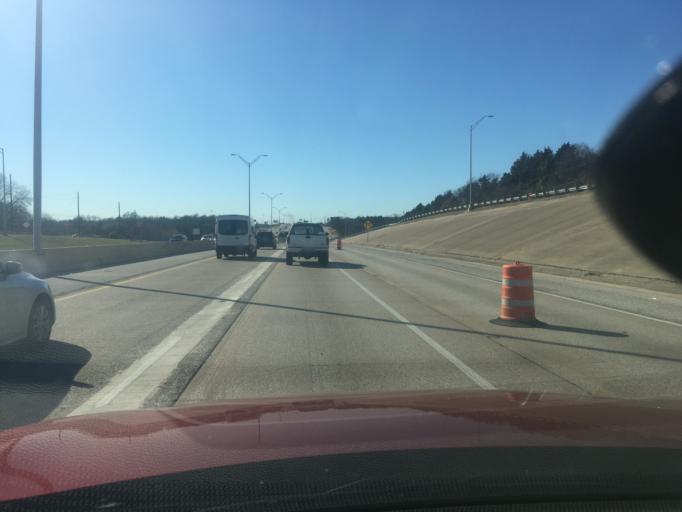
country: US
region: Texas
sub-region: Dallas County
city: Duncanville
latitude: 32.6705
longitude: -96.8627
